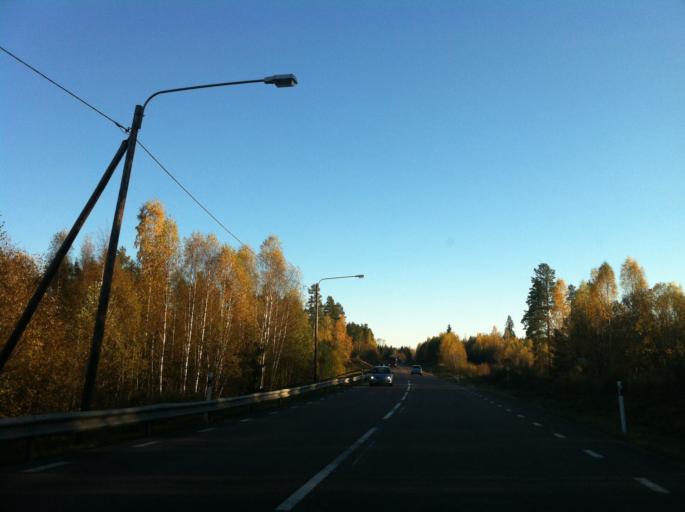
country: SE
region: Dalarna
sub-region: Faluns Kommun
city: Grycksbo
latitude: 60.6625
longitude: 15.5477
